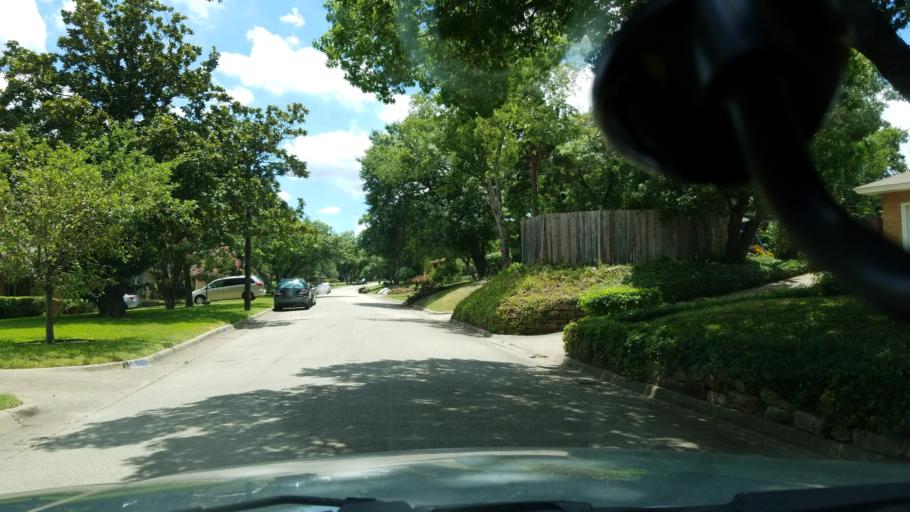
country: US
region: Texas
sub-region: Dallas County
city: Cockrell Hill
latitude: 32.7049
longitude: -96.8763
